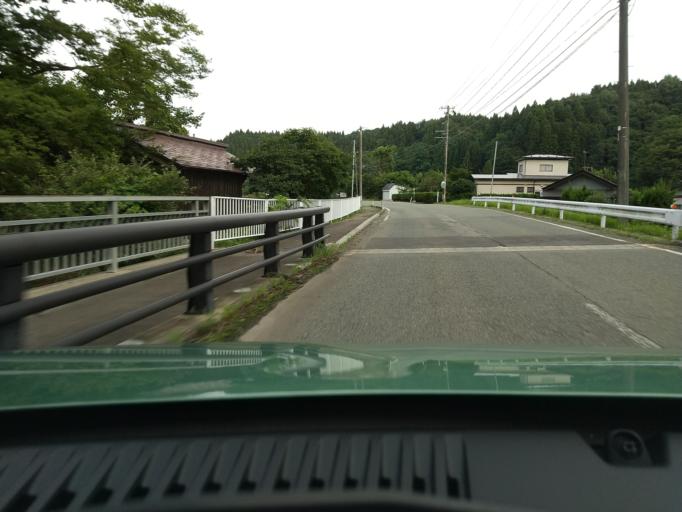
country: JP
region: Akita
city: Akita Shi
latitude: 39.7902
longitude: 140.1130
